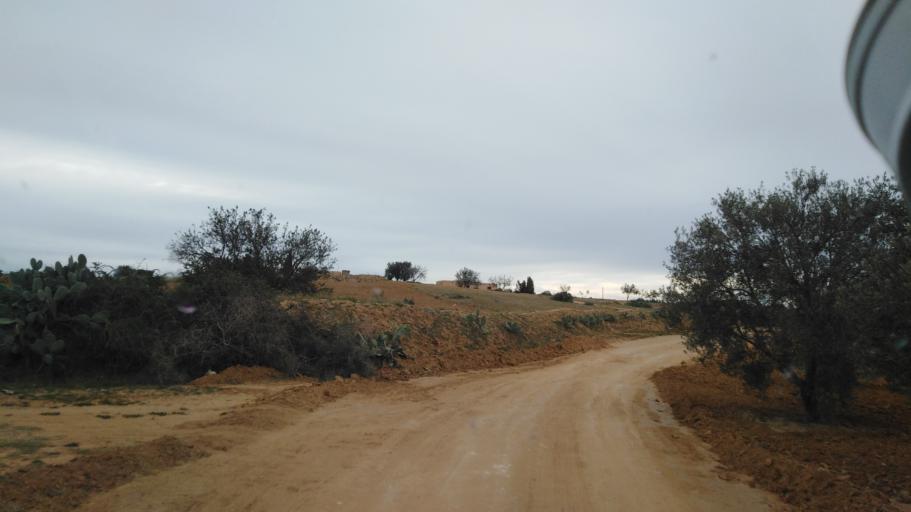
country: TN
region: Safaqis
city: Bi'r `Ali Bin Khalifah
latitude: 34.7670
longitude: 10.3763
